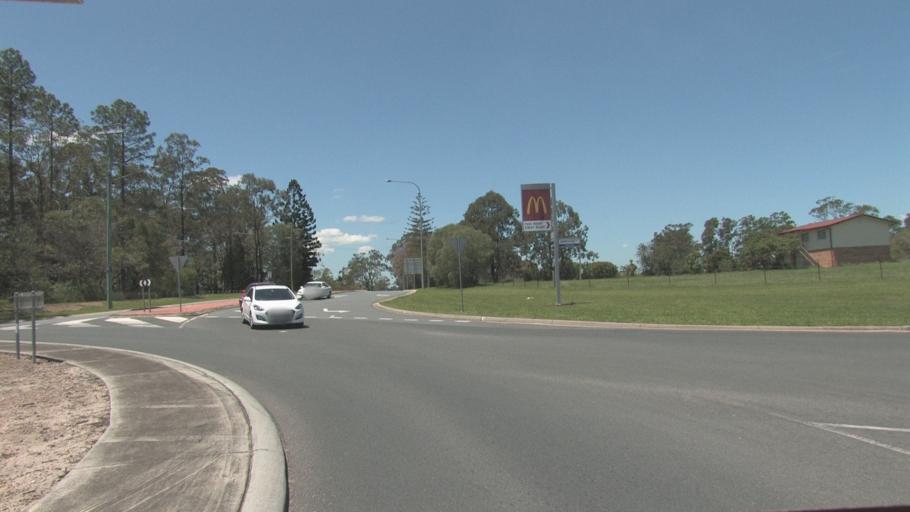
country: AU
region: Queensland
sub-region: Logan
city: Park Ridge South
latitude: -27.6985
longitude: 153.0403
